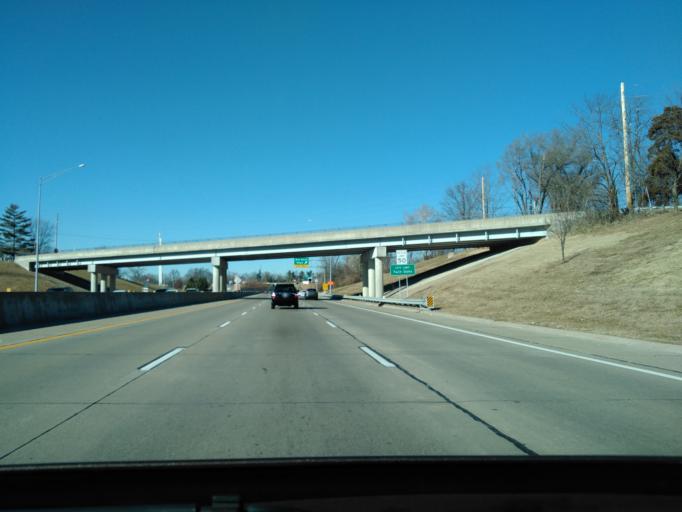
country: US
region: Missouri
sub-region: Saint Louis County
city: Valley Park
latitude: 38.5633
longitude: -90.4968
